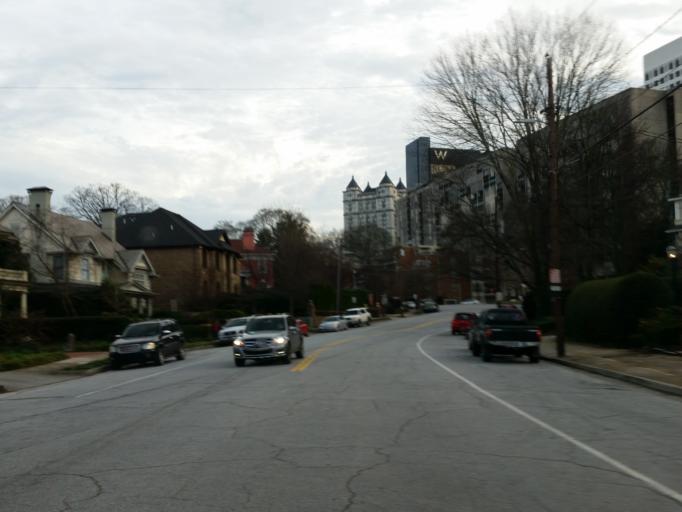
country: US
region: Georgia
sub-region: Fulton County
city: Atlanta
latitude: 33.7902
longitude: -84.3829
